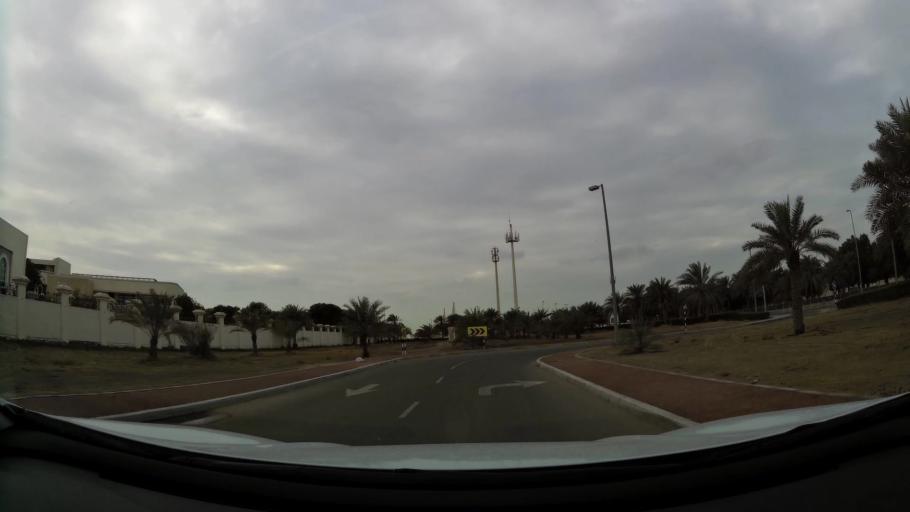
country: AE
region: Abu Dhabi
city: Abu Dhabi
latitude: 24.4312
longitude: 54.3738
